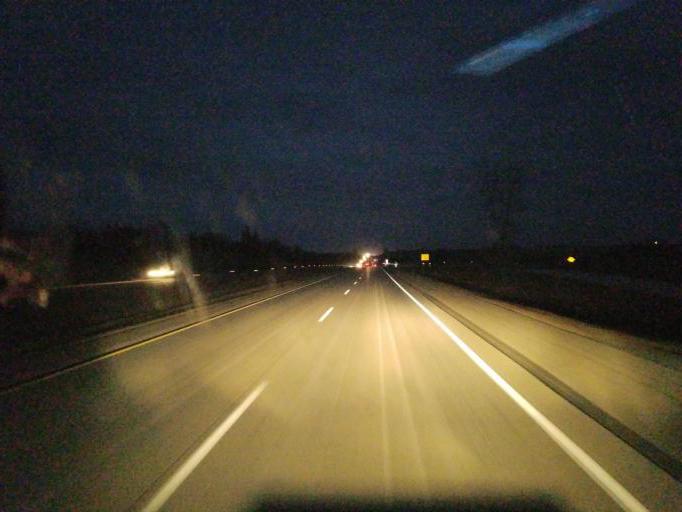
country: US
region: Iowa
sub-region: Guthrie County
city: Guthrie Center
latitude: 41.4960
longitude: -94.5135
